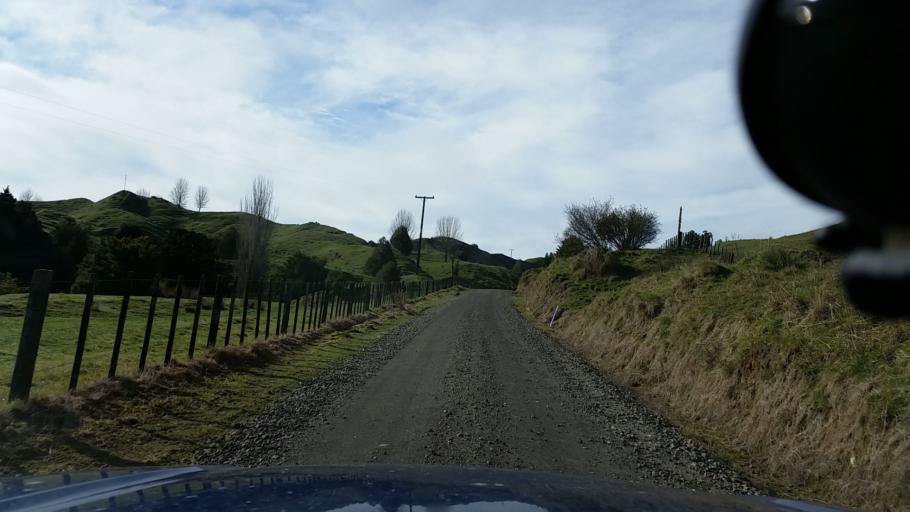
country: NZ
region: Taranaki
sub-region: New Plymouth District
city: Waitara
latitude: -39.0337
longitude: 174.7714
